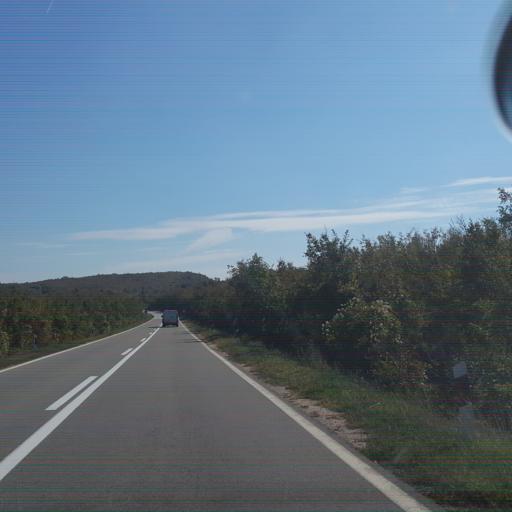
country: RS
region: Central Serbia
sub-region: Zajecarski Okrug
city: Knjazevac
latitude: 43.4972
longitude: 22.2191
